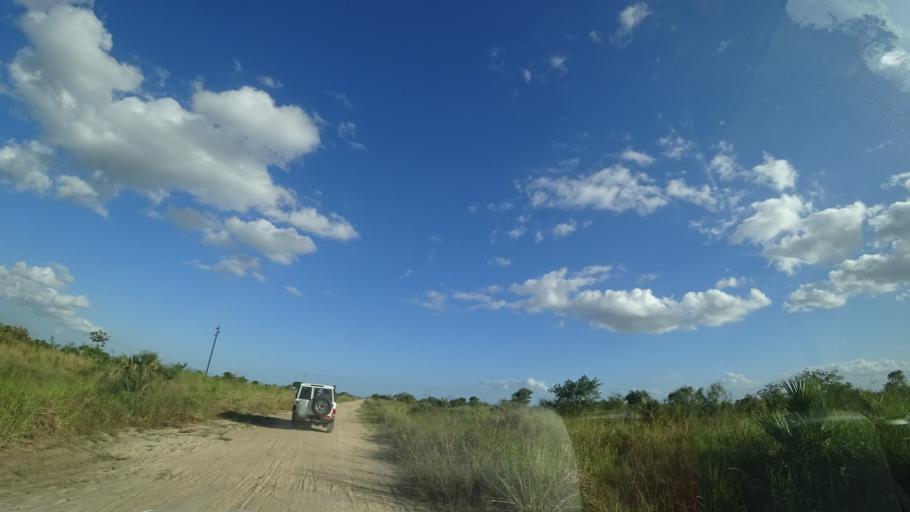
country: MZ
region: Sofala
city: Dondo
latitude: -19.4295
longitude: 34.5608
